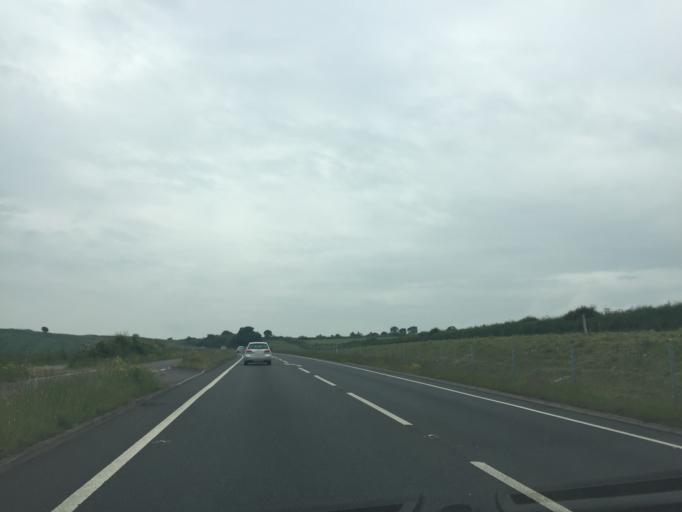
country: GB
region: England
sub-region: Dorset
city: Dorchester
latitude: 50.6761
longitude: -2.4651
